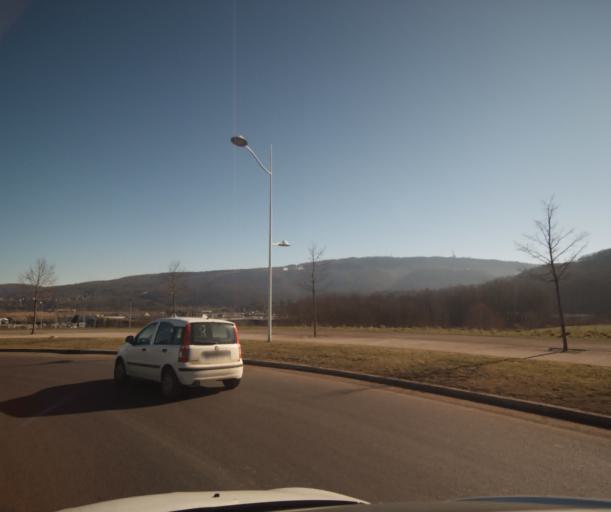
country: FR
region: Franche-Comte
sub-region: Departement du Doubs
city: Thise
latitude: 47.2626
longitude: 6.0612
